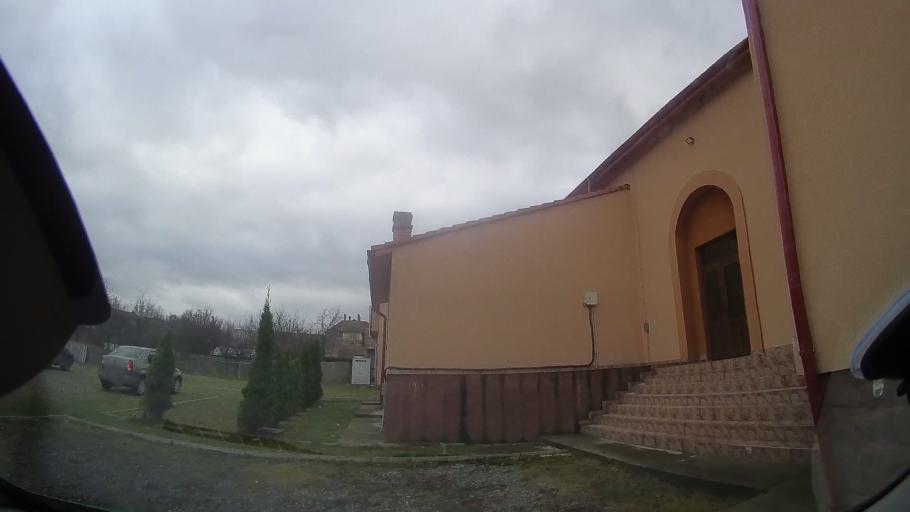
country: RO
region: Cluj
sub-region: Comuna Calatele
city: Calatele
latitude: 46.7682
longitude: 23.0092
